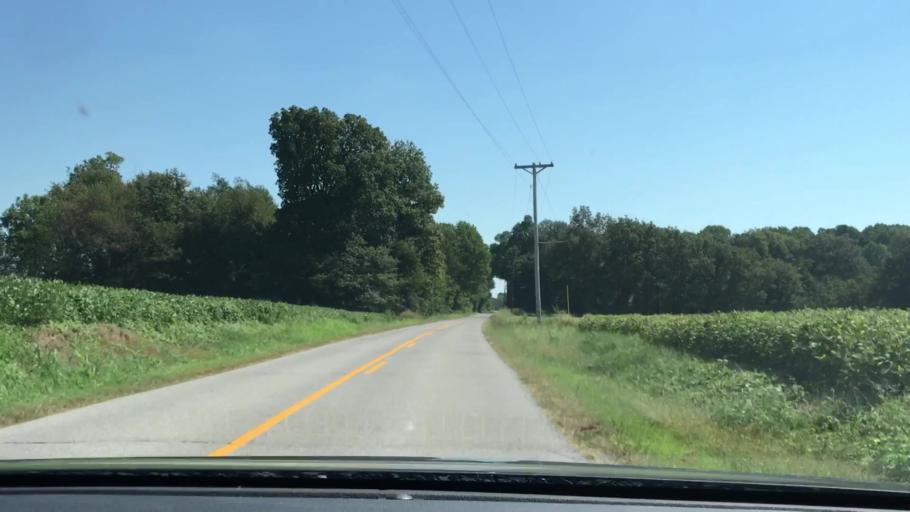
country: US
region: Kentucky
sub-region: Fulton County
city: Fulton
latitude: 36.5223
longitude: -88.8999
